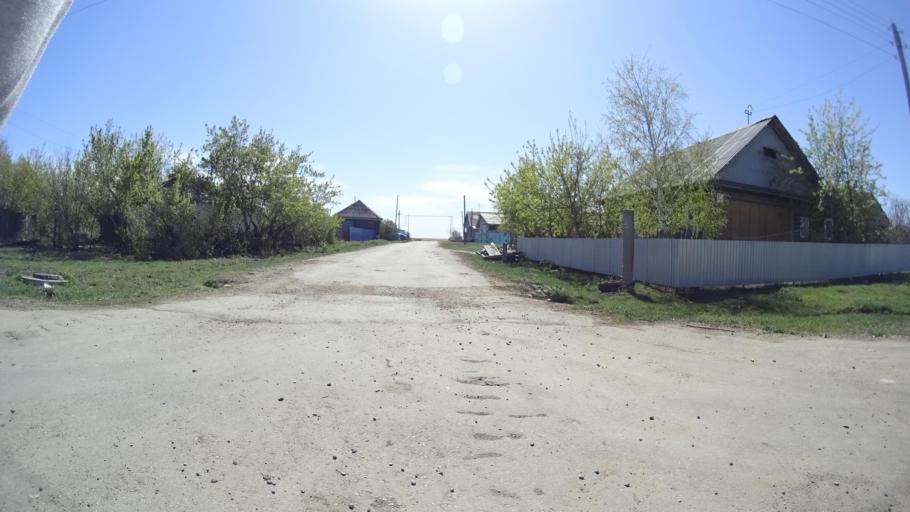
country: RU
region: Chelyabinsk
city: Chesma
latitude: 53.7990
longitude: 61.0228
